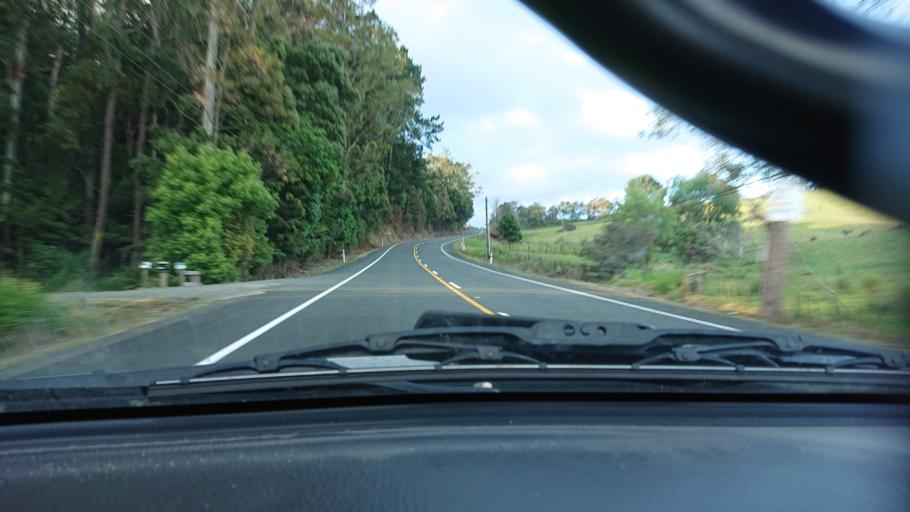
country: NZ
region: Auckland
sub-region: Auckland
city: Parakai
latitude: -36.5278
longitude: 174.4543
